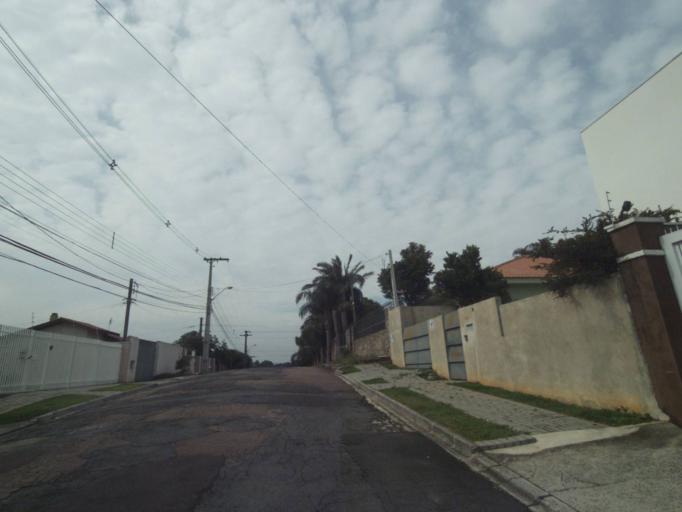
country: BR
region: Parana
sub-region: Curitiba
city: Curitiba
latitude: -25.4100
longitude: -49.2948
